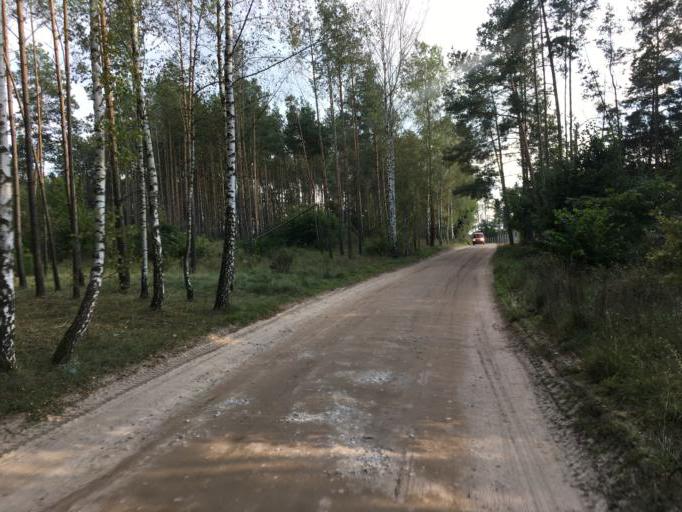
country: PL
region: Kujawsko-Pomorskie
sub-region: Powiat tucholski
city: Tuchola
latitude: 53.6029
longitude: 17.9106
